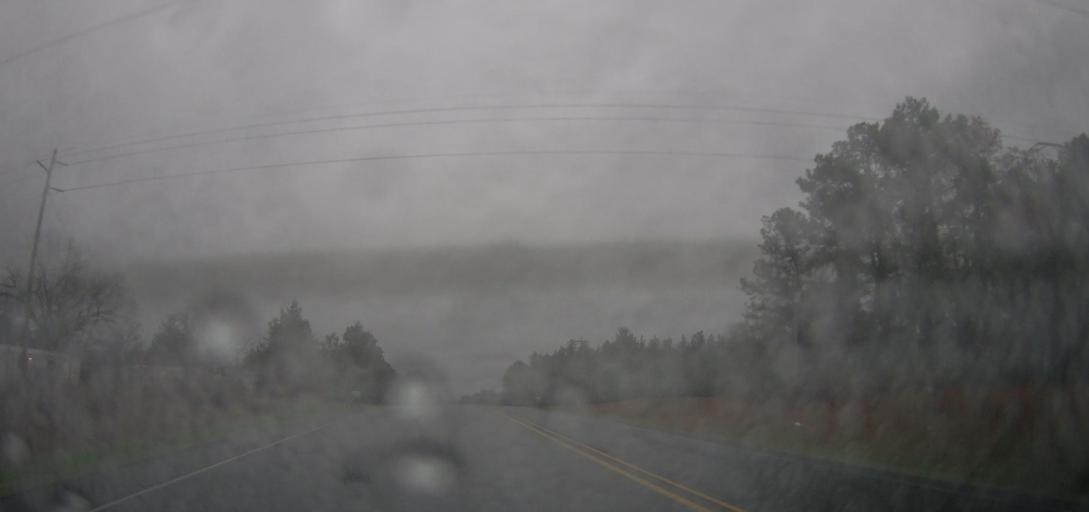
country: US
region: Alabama
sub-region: Autauga County
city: Pine Level
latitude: 32.5866
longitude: -86.6971
